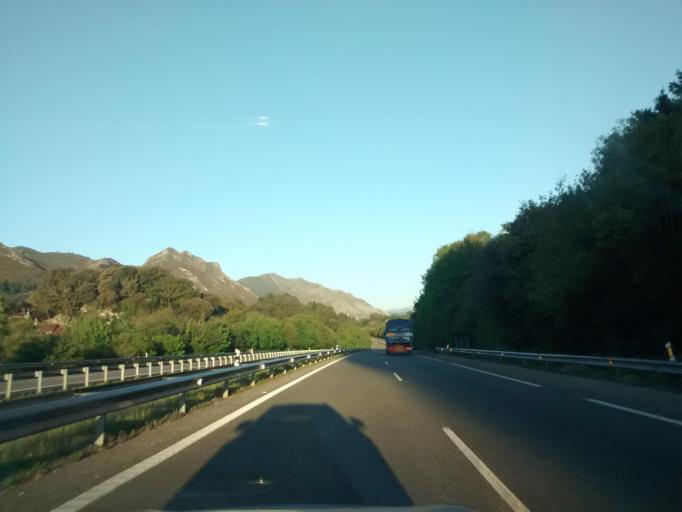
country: ES
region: Asturias
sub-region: Province of Asturias
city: Ribadesella
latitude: 43.4442
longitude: -4.9336
